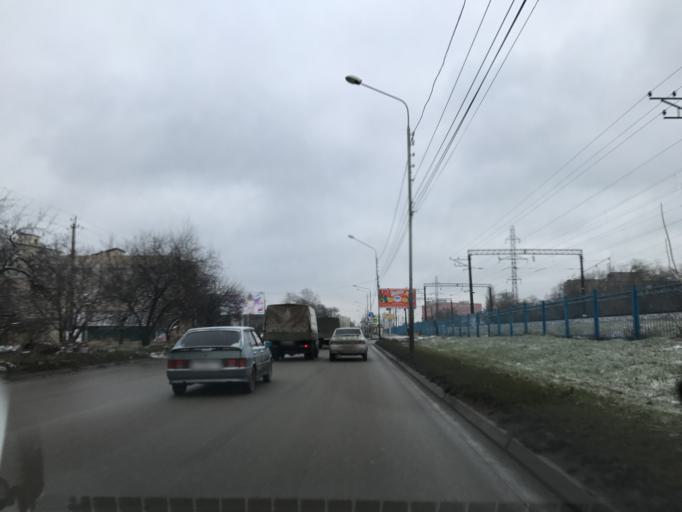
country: RU
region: Rostov
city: Rostov-na-Donu
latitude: 47.2444
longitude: 39.7218
